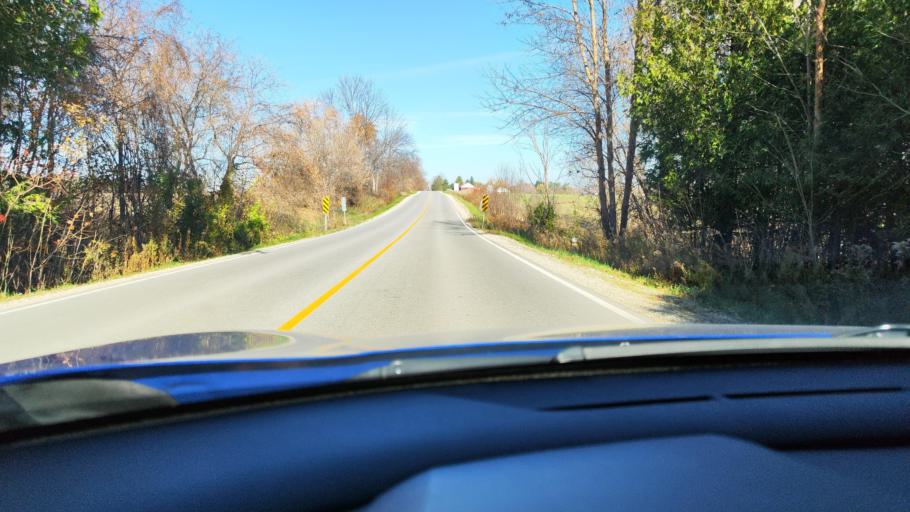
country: CA
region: Ontario
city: Wasaga Beach
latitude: 44.4165
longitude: -80.0615
